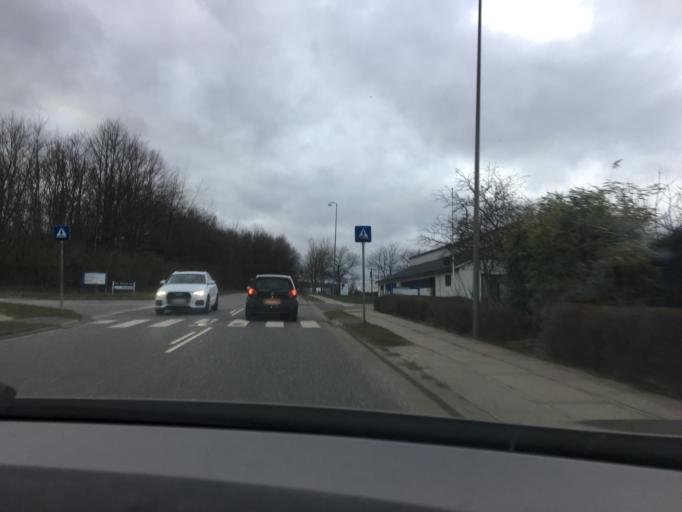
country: DK
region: South Denmark
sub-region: Vejle Kommune
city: Vejle
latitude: 55.7251
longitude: 9.5979
